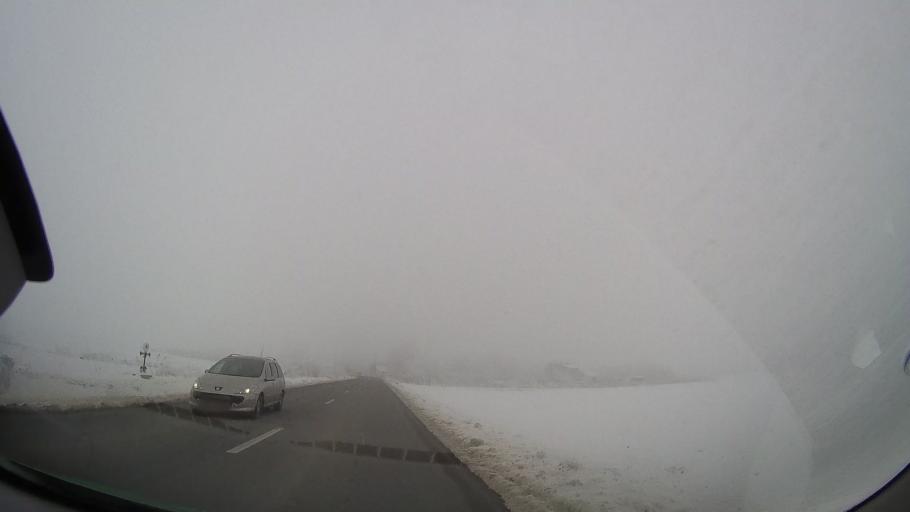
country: RO
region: Iasi
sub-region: Comuna Mogosesti-Siret
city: Mogosesti-Siret
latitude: 47.1561
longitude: 26.7765
